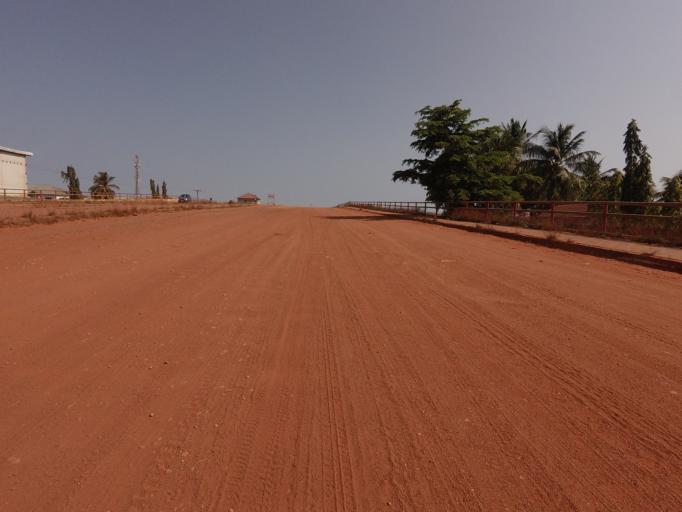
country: GH
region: Greater Accra
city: Teshi Old Town
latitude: 5.6205
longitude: -0.1247
